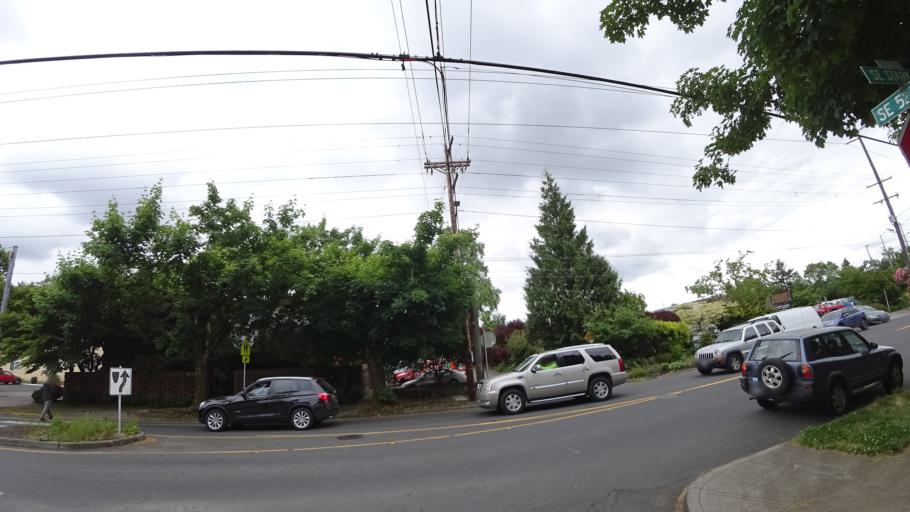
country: US
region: Oregon
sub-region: Multnomah County
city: Lents
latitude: 45.5194
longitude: -122.6103
